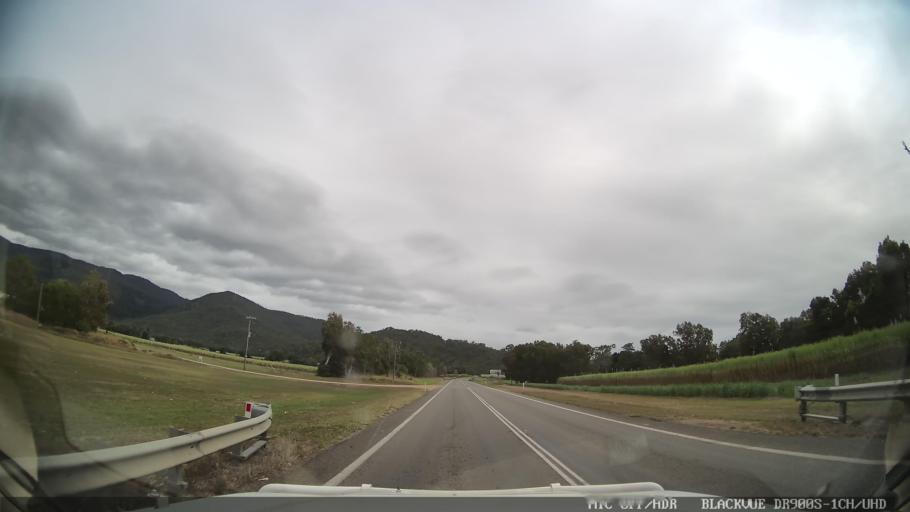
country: AU
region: Queensland
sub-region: Hinchinbrook
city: Ingham
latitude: -18.8633
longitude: 146.1732
